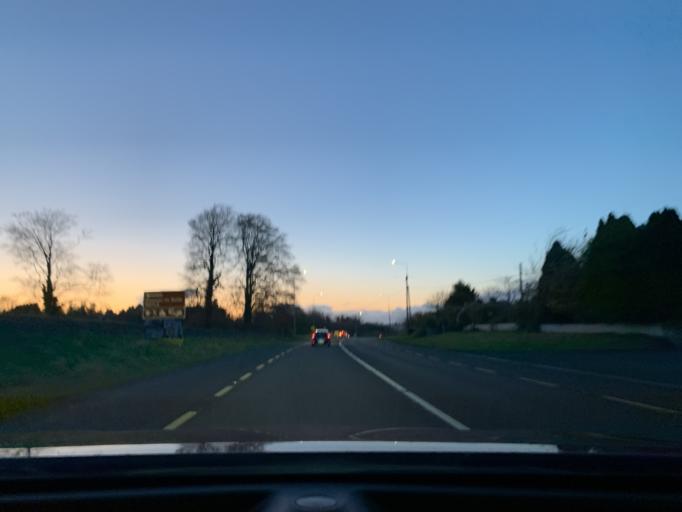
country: IE
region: Connaught
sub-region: Roscommon
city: Boyle
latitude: 53.9693
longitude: -8.2594
